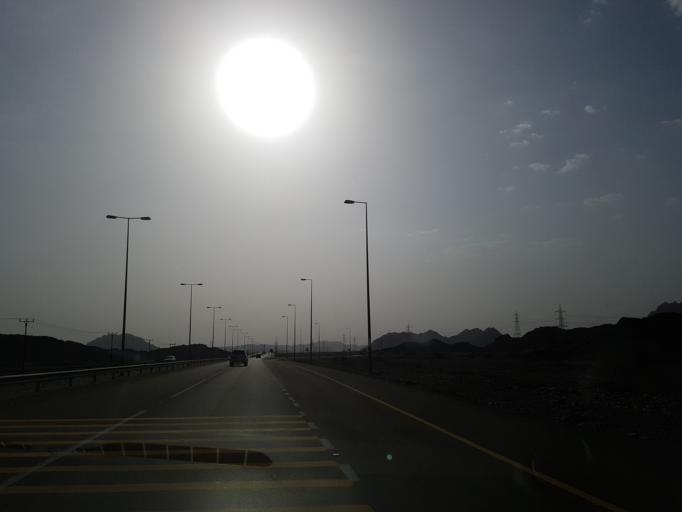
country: OM
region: Al Buraimi
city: Al Buraymi
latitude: 24.2468
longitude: 56.0232
